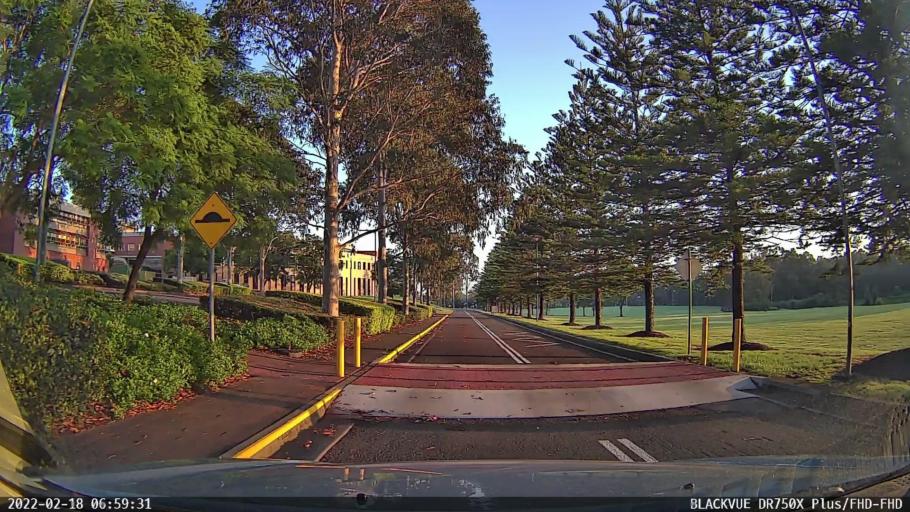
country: AU
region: New South Wales
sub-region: Penrith Municipality
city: Kingswood Park
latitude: -33.7680
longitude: 150.7302
